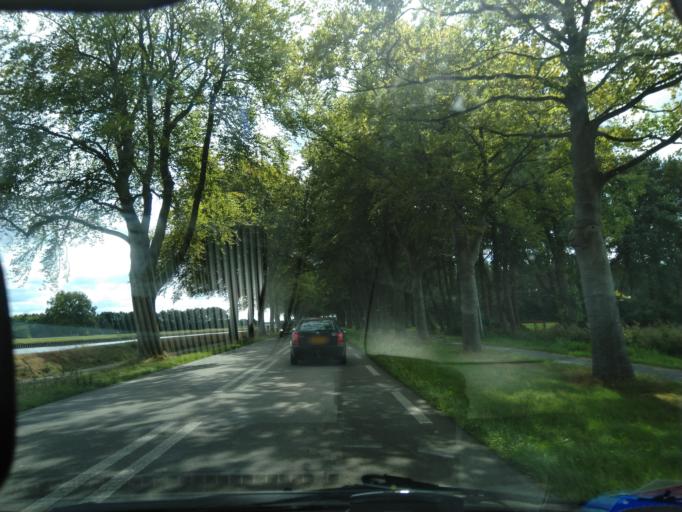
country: NL
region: Drenthe
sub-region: Gemeente Tynaarlo
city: Tynaarlo
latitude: 53.1079
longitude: 6.6044
